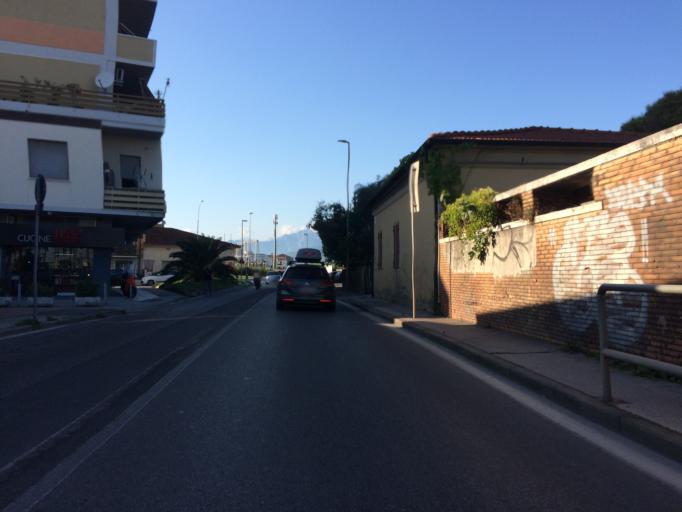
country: IT
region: Tuscany
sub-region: Provincia di Lucca
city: Viareggio
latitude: 43.8768
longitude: 10.2515
